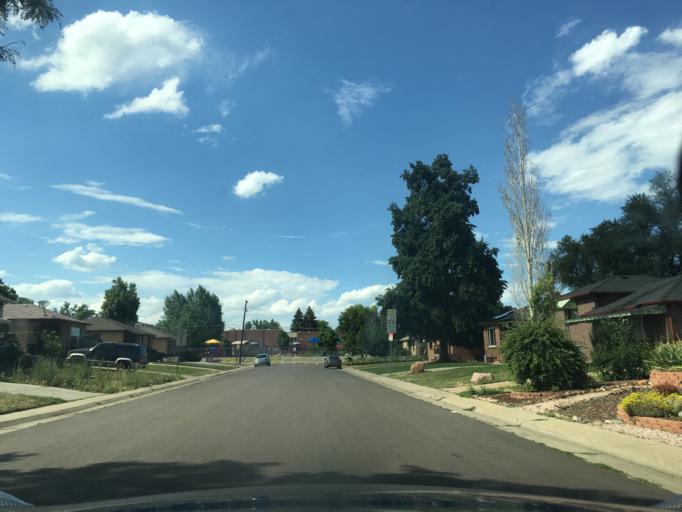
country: US
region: Colorado
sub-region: Jefferson County
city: Lakewood
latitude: 39.6871
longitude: -105.0470
